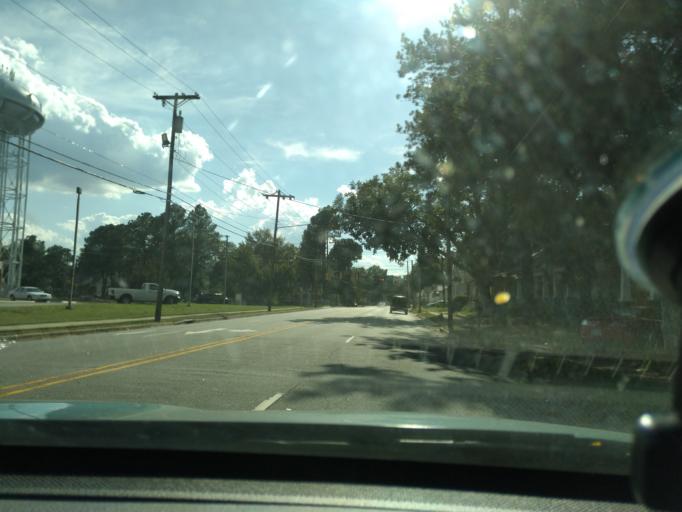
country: US
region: North Carolina
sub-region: Nash County
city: Rocky Mount
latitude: 35.9381
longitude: -77.7918
